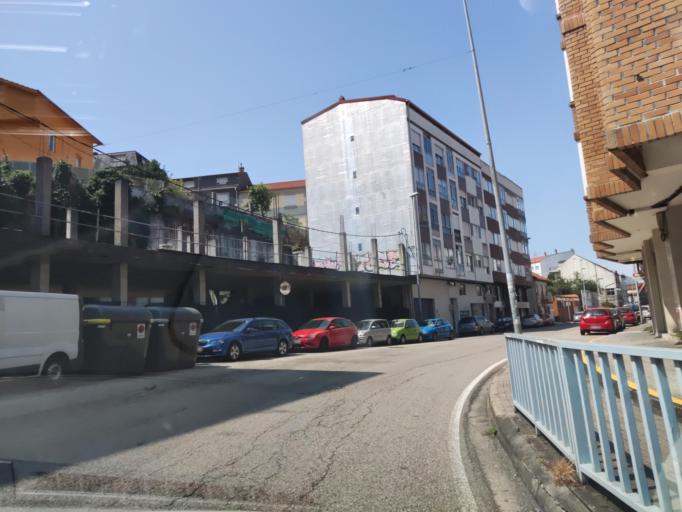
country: ES
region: Galicia
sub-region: Provincia de Pontevedra
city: Redondela
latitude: 42.2702
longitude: -8.6665
